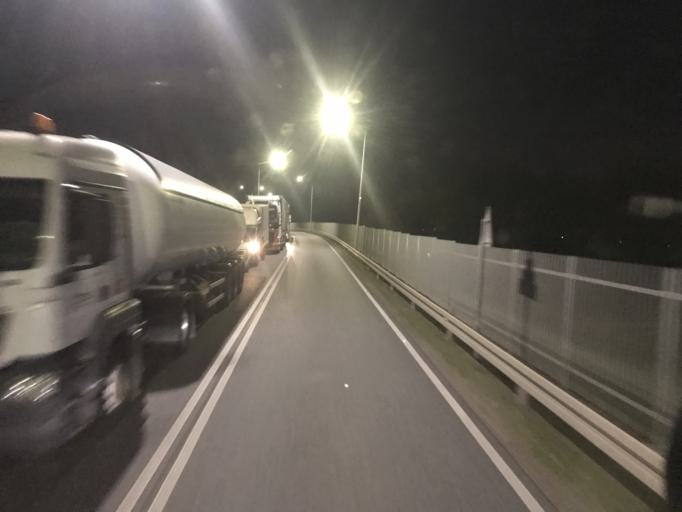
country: PL
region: Lublin Voivodeship
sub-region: Powiat bialski
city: Terespol
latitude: 52.0812
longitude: 23.5300
